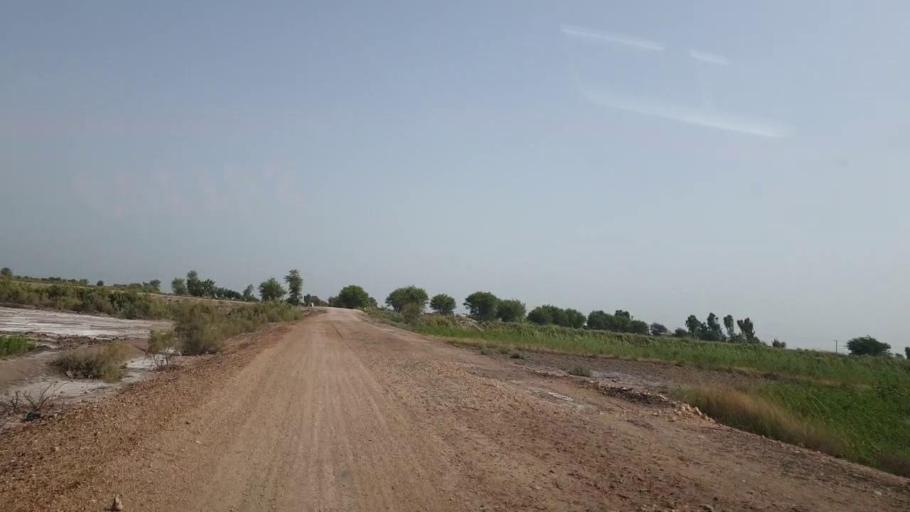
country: PK
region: Sindh
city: Sakrand
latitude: 26.2880
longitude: 68.2265
